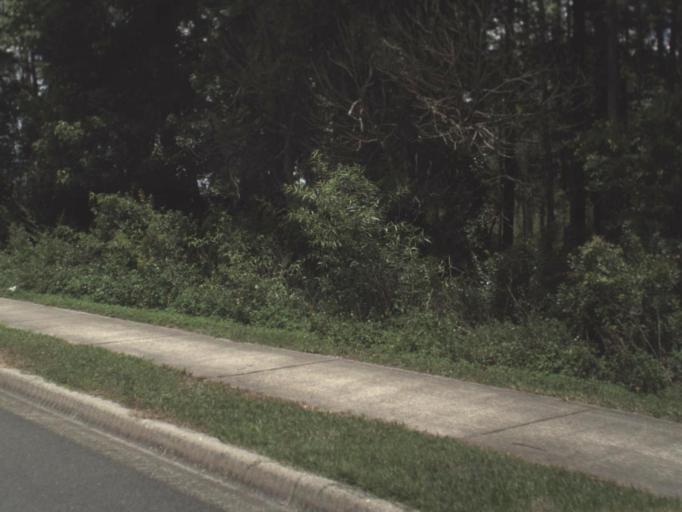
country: US
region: Florida
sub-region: Alachua County
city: Gainesville
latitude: 29.6885
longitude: -82.3161
